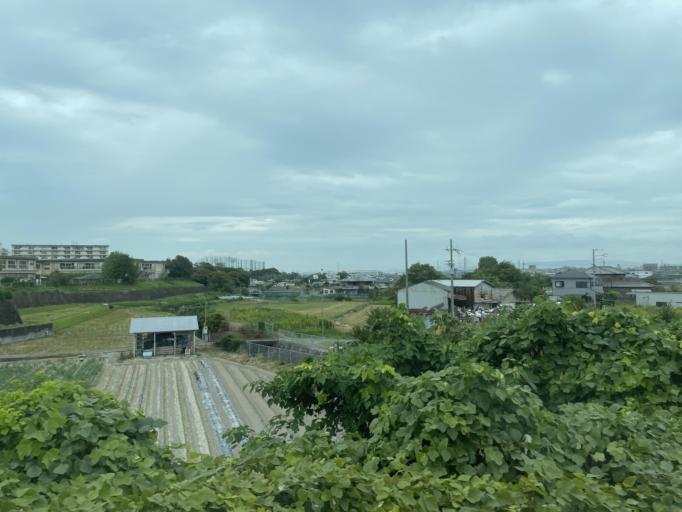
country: JP
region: Osaka
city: Kaizuka
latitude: 34.3704
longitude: 135.2956
